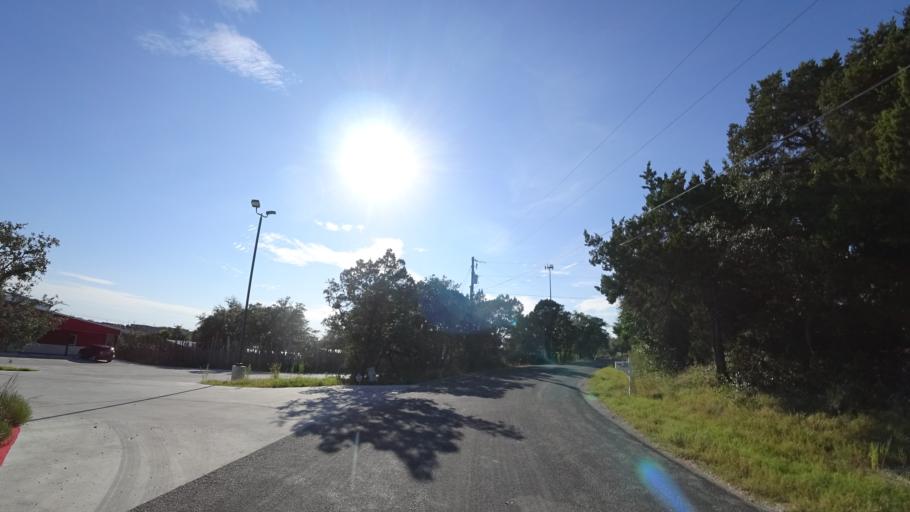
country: US
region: Texas
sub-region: Travis County
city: Barton Creek
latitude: 30.2330
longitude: -97.9266
